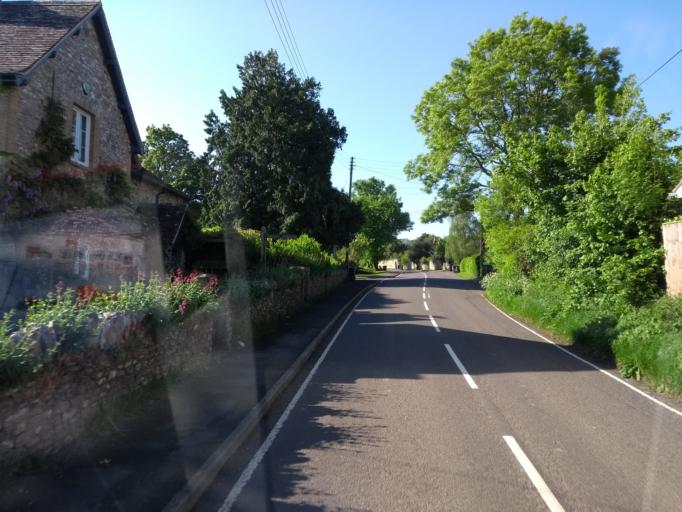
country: GB
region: England
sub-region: Somerset
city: Taunton
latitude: 50.9722
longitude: -3.0951
